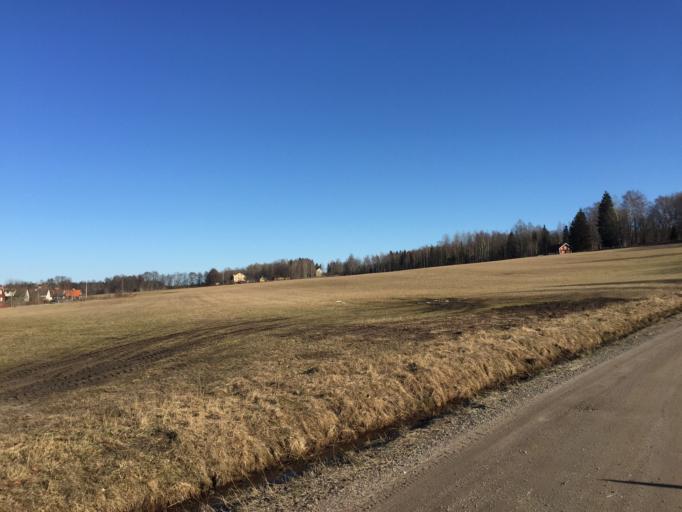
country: SE
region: OErebro
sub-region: Orebro Kommun
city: Odensbacken
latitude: 59.0100
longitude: 15.5836
